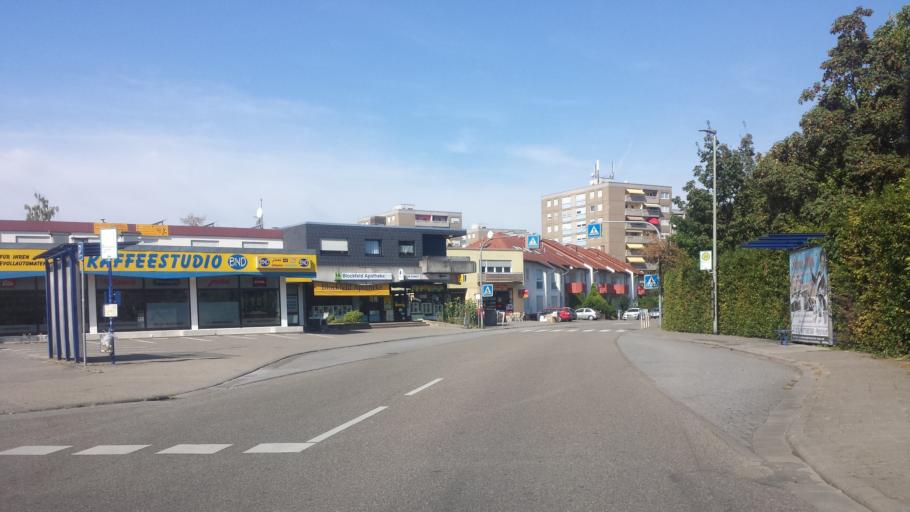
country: DE
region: Rheinland-Pfalz
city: Mutterstadt
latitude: 49.4384
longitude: 8.3511
